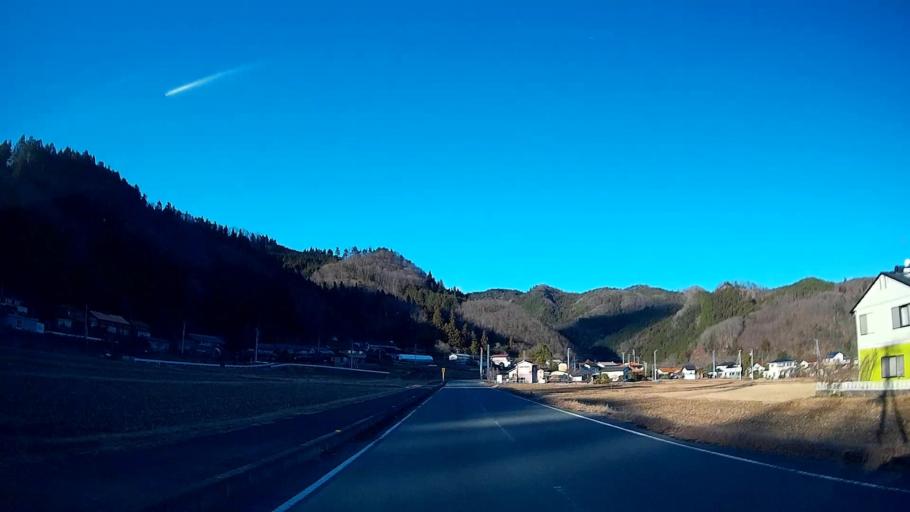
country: JP
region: Saitama
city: Chichibu
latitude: 36.0411
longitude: 139.0111
